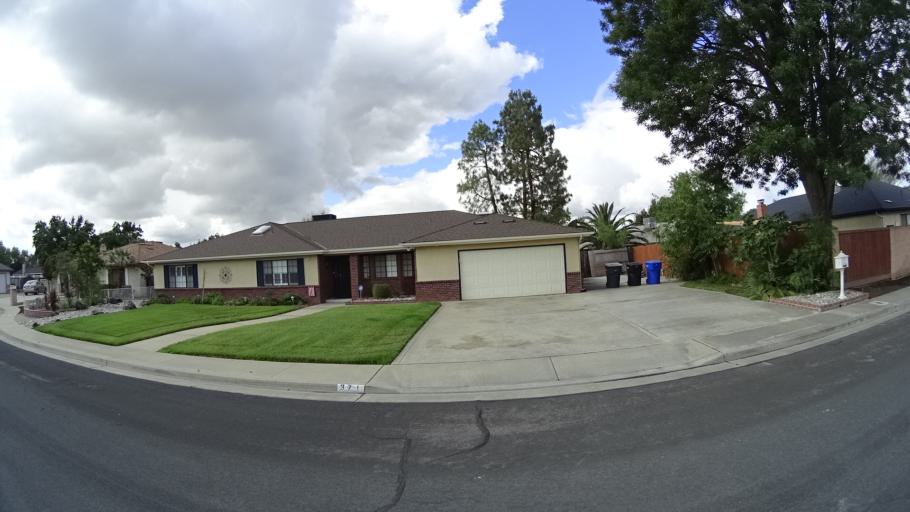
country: US
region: California
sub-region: Kings County
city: Lucerne
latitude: 36.3606
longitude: -119.6503
